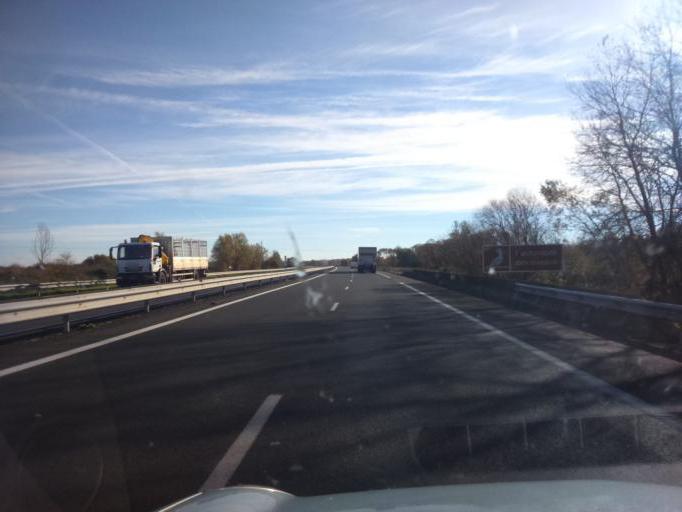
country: FR
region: Poitou-Charentes
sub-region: Departement de la Charente-Maritime
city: Breuil-Magne
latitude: 45.9583
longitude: -0.9404
